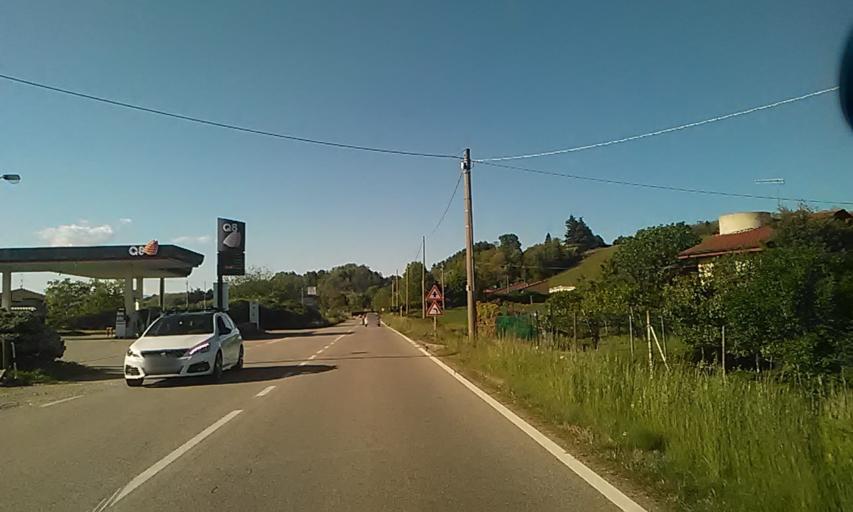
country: IT
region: Piedmont
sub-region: Provincia di Novara
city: Ghemme
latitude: 45.5945
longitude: 8.4266
